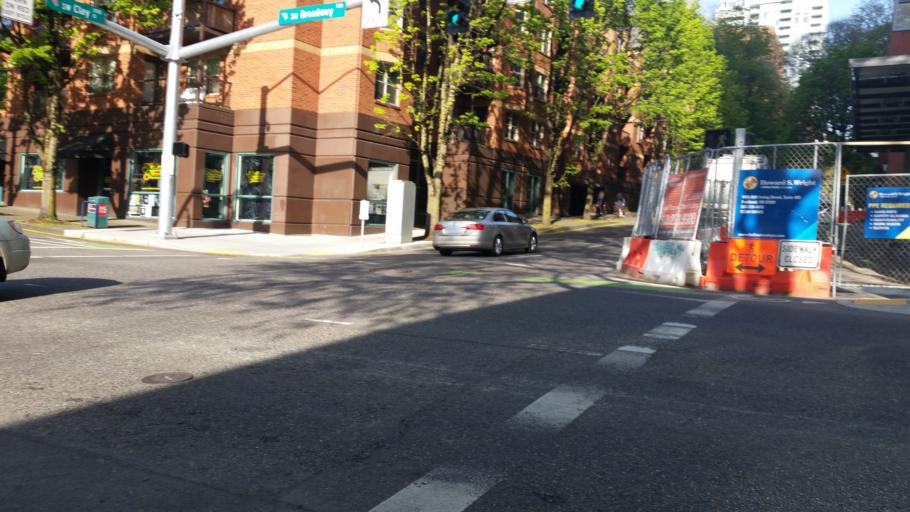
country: US
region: Oregon
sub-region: Multnomah County
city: Portland
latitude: 45.5141
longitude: -122.6825
